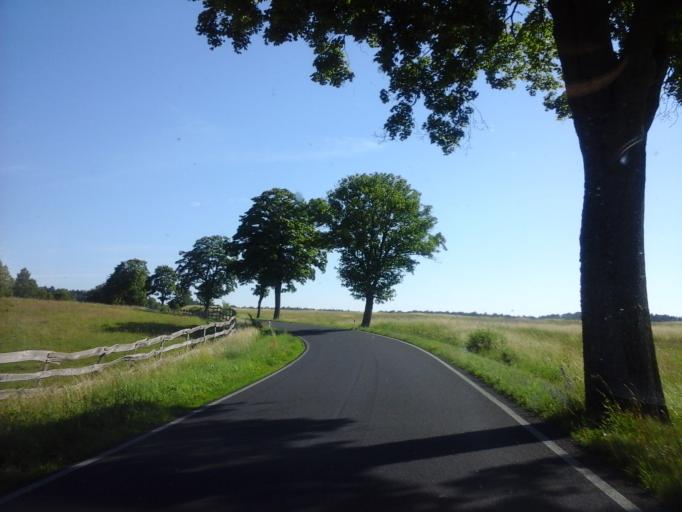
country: PL
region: West Pomeranian Voivodeship
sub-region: Powiat drawski
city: Zlocieniec
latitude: 53.6090
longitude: 15.9197
